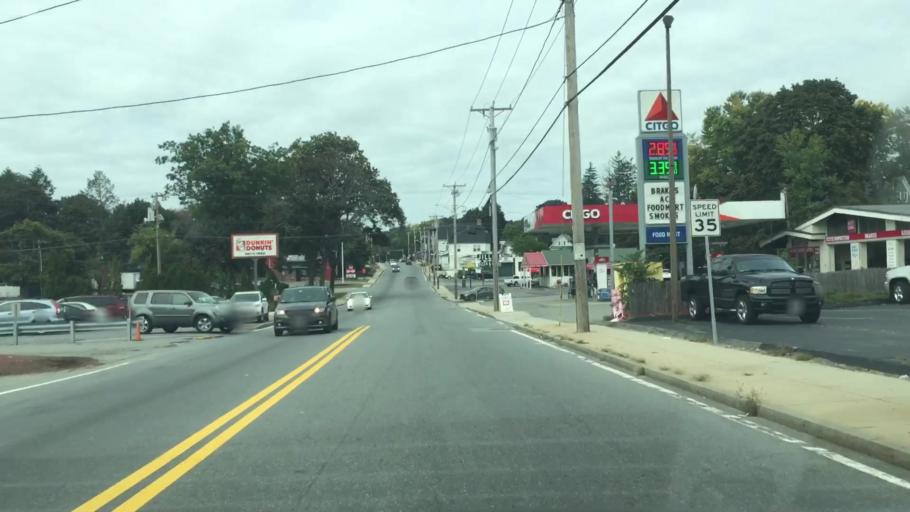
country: US
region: Massachusetts
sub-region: Middlesex County
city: Lowell
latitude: 42.6310
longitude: -71.2819
